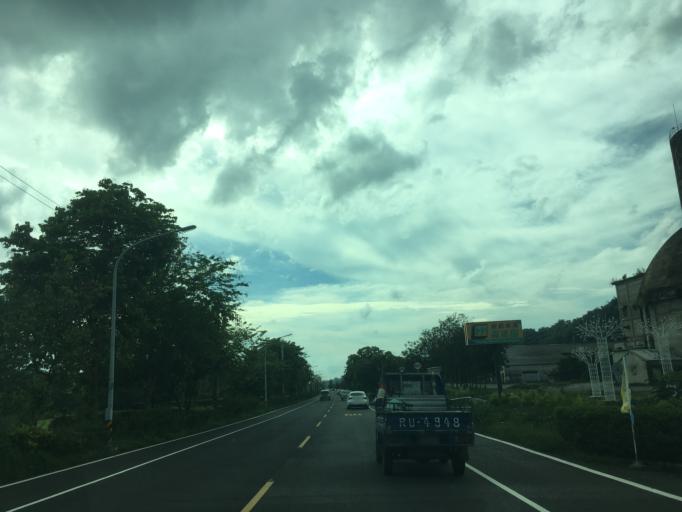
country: TW
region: Taiwan
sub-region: Chiayi
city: Jiayi Shi
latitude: 23.4438
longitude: 120.5909
